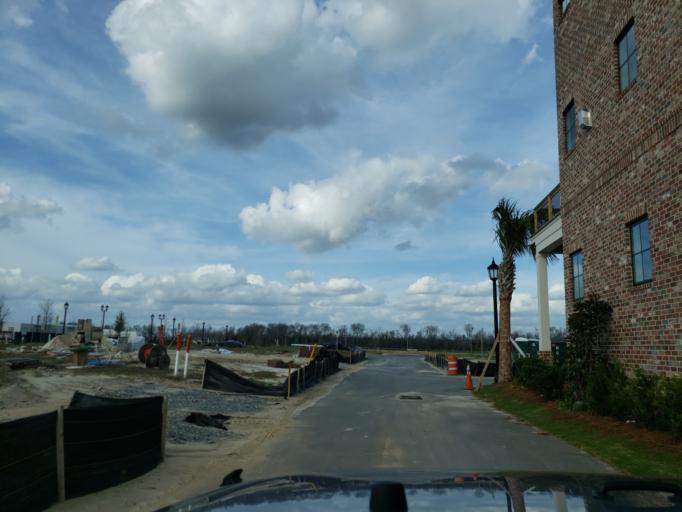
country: US
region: Georgia
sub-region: Chatham County
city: Savannah
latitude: 32.0765
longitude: -81.0774
